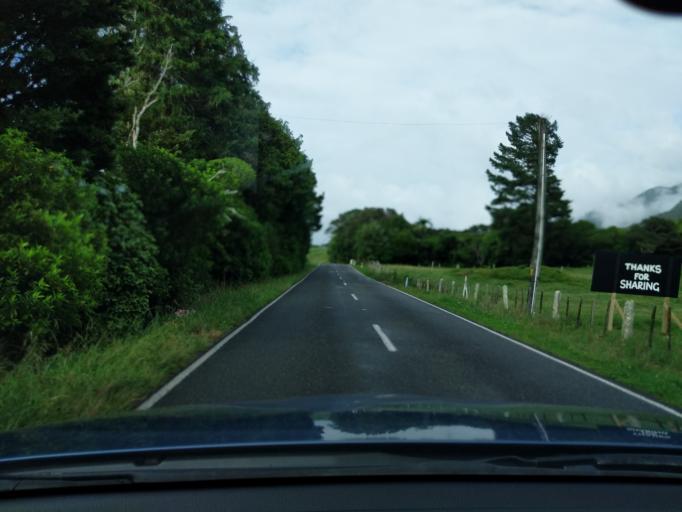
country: NZ
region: Tasman
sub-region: Tasman District
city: Takaka
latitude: -40.6271
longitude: 172.6745
